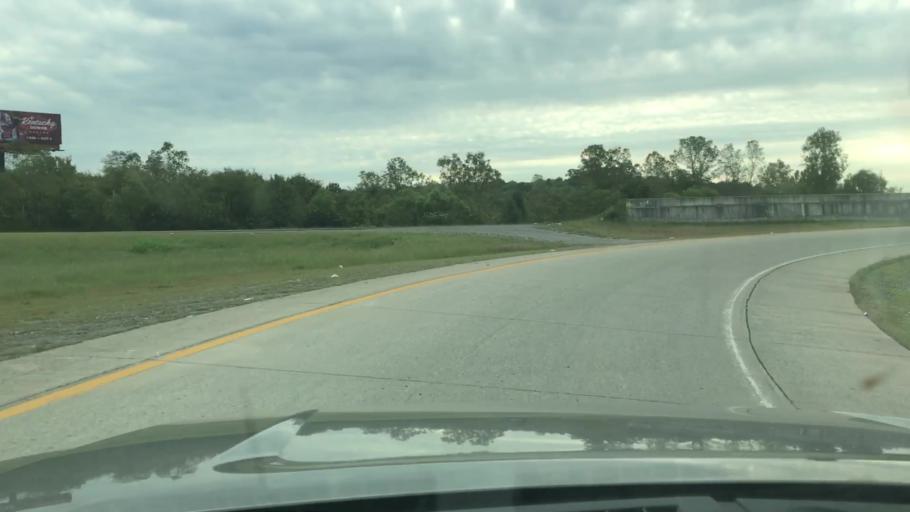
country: US
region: Tennessee
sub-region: Davidson County
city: Nashville
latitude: 36.2375
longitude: -86.7569
